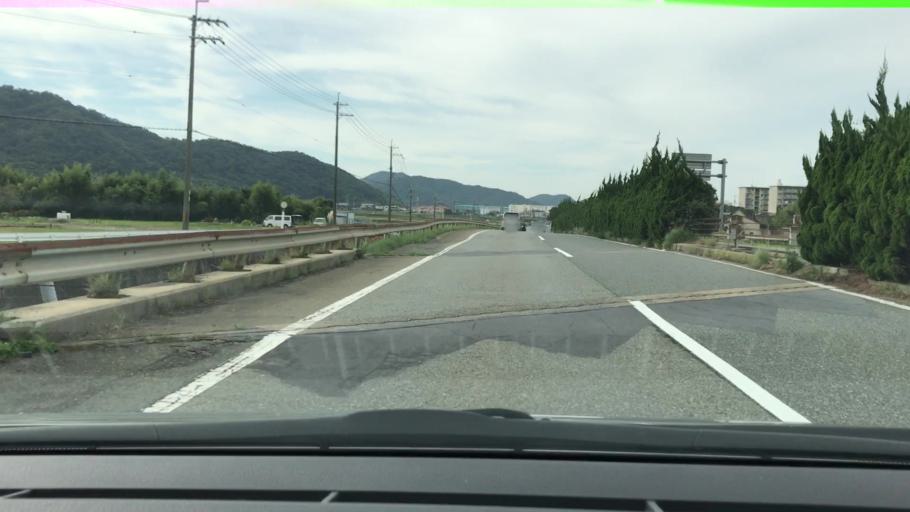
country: JP
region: Hyogo
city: Himeji
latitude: 34.9023
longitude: 134.7521
